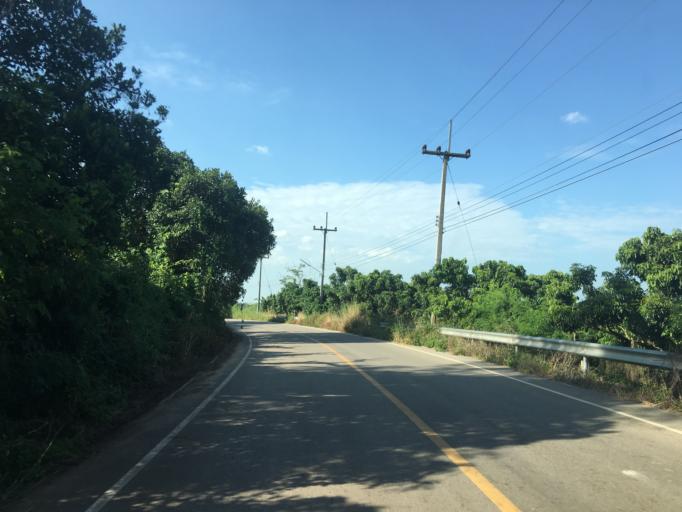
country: TH
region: Chiang Rai
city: Pa Daet
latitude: 19.4295
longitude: 100.0145
